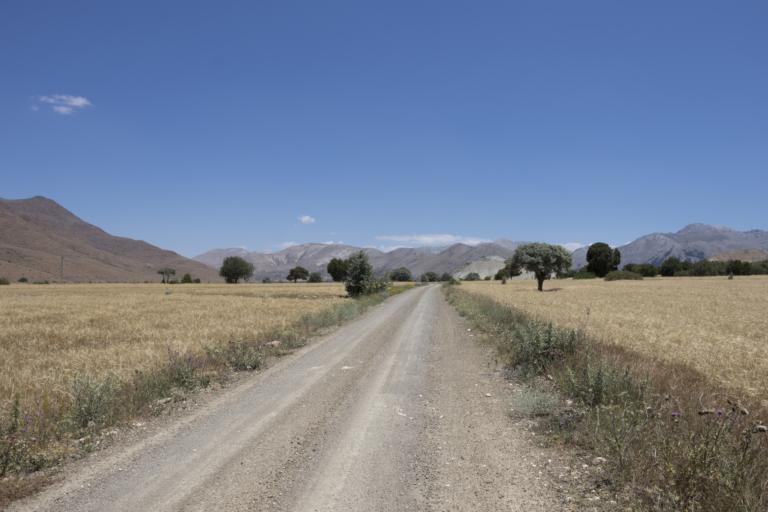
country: TR
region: Kayseri
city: Toklar
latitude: 38.3569
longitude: 36.0176
